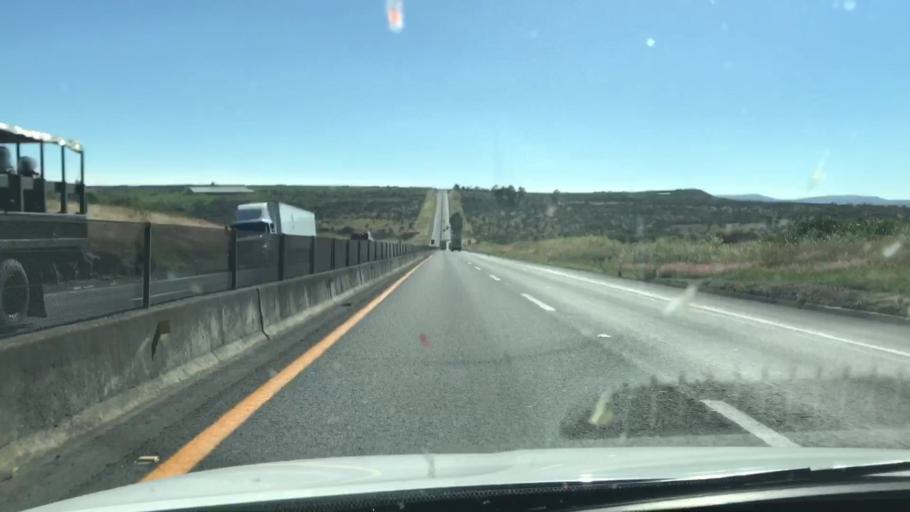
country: MX
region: Jalisco
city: Valle de Guadalupe
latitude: 21.0439
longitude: -102.5390
